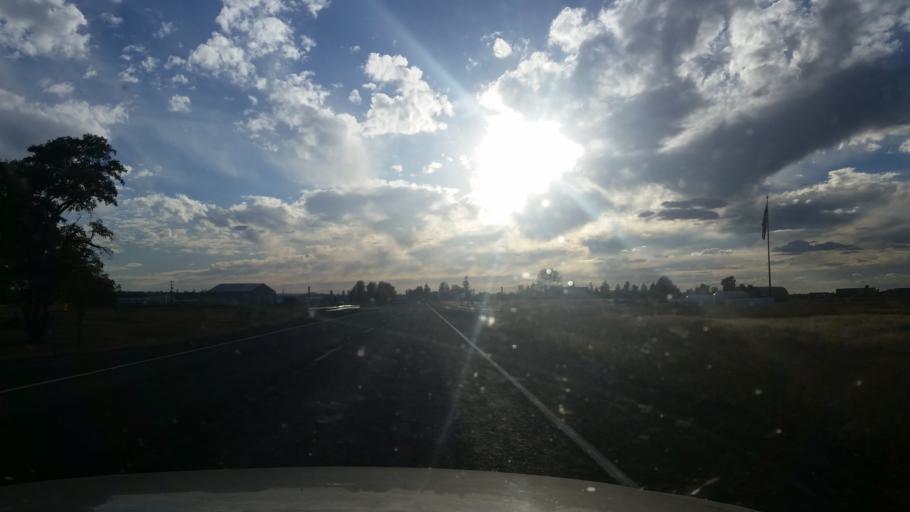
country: US
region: Washington
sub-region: Spokane County
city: Cheney
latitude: 47.4656
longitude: -117.6441
